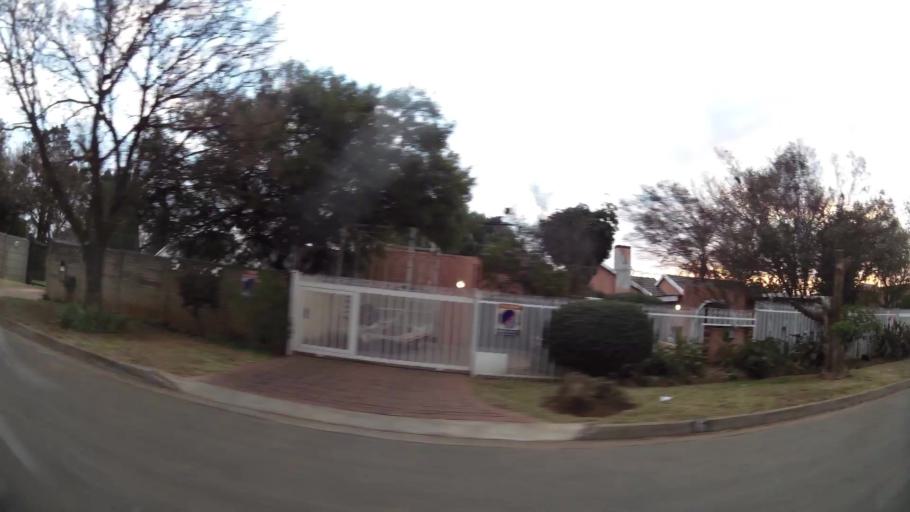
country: ZA
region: Gauteng
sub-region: Ekurhuleni Metropolitan Municipality
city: Germiston
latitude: -26.2014
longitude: 28.1423
